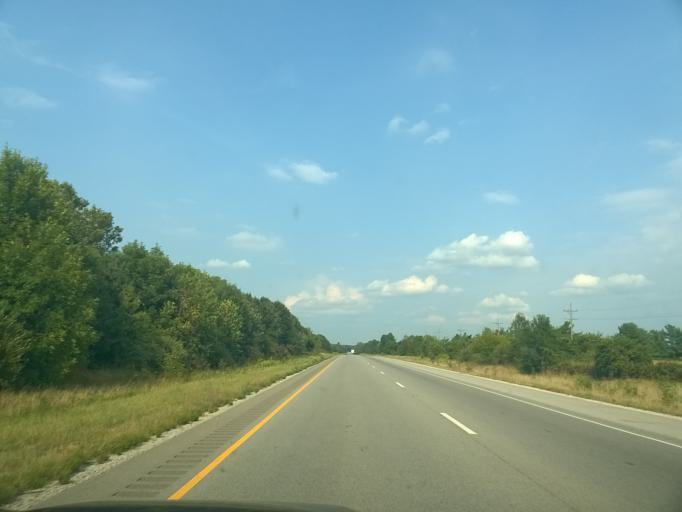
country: US
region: Indiana
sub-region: Vigo County
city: Seelyville
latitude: 39.4332
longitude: -87.2929
